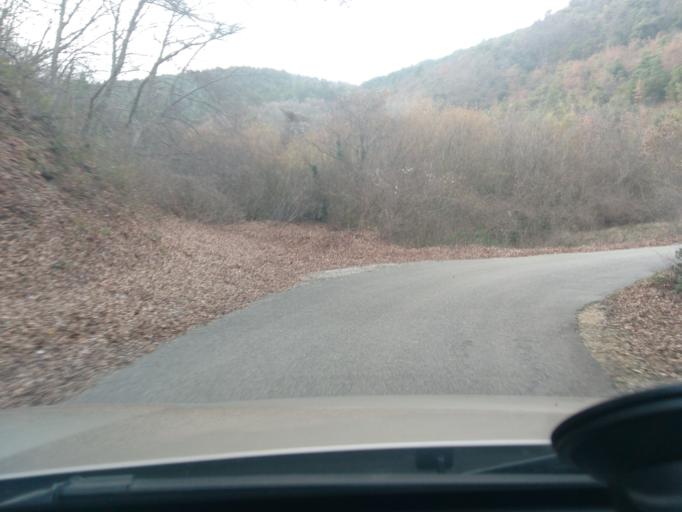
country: FR
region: Rhone-Alpes
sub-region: Departement de l'Ardeche
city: Cruas
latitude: 44.6611
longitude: 4.7389
